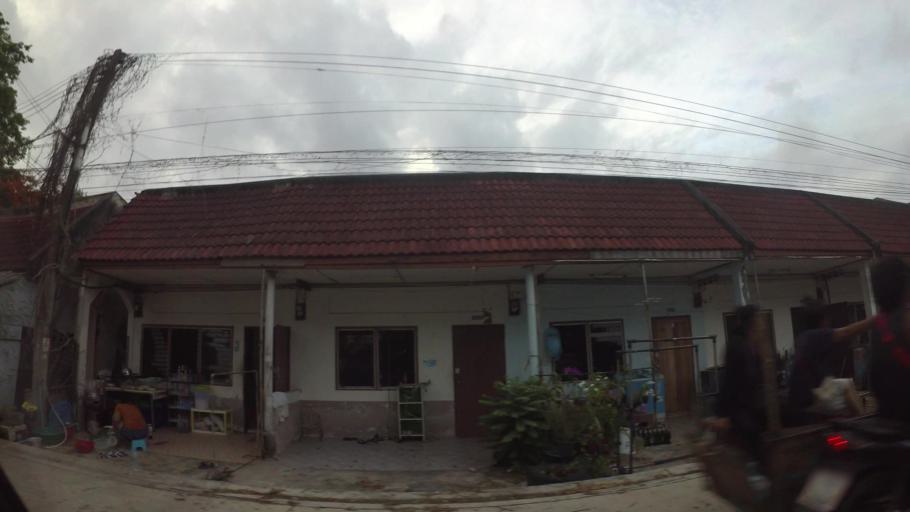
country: TH
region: Rayong
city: Rayong
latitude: 12.6720
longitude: 101.2667
